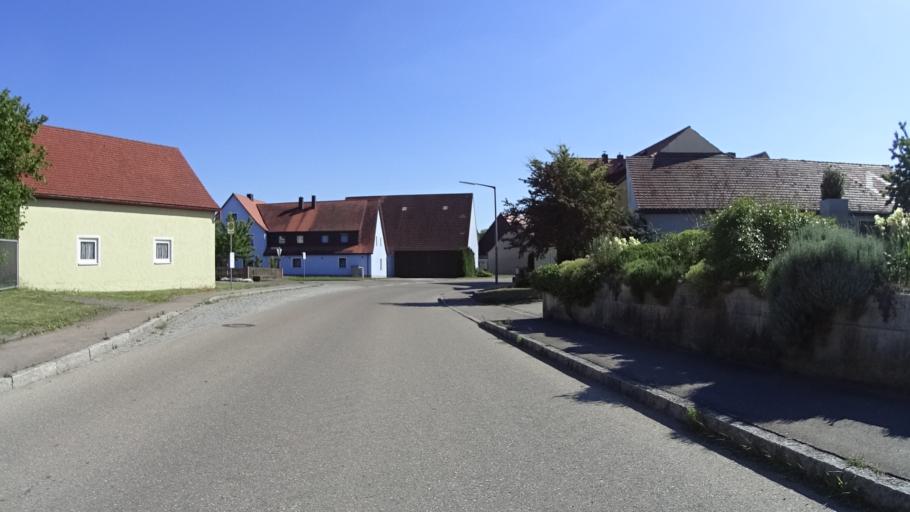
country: DE
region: Bavaria
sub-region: Regierungsbezirk Mittelfranken
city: Dombuhl
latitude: 49.2181
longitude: 10.3052
